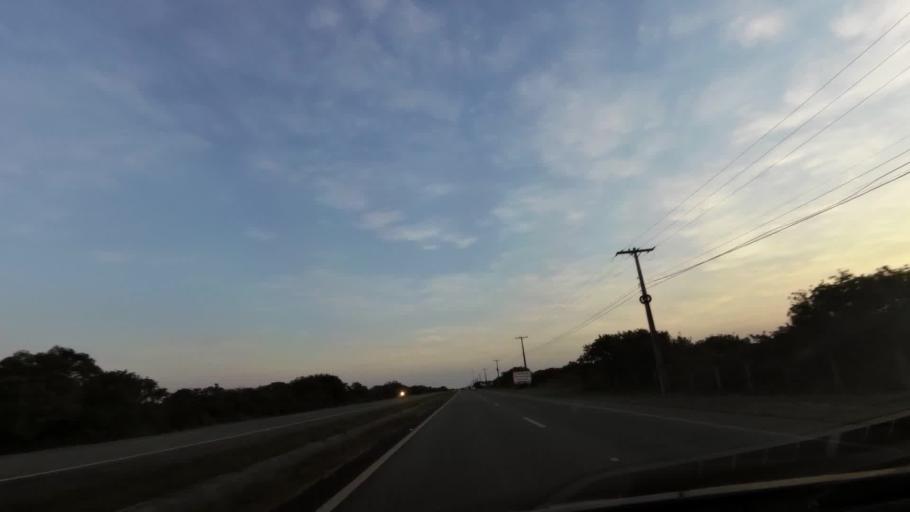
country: BR
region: Espirito Santo
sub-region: Guarapari
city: Guarapari
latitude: -20.5669
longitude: -40.4101
